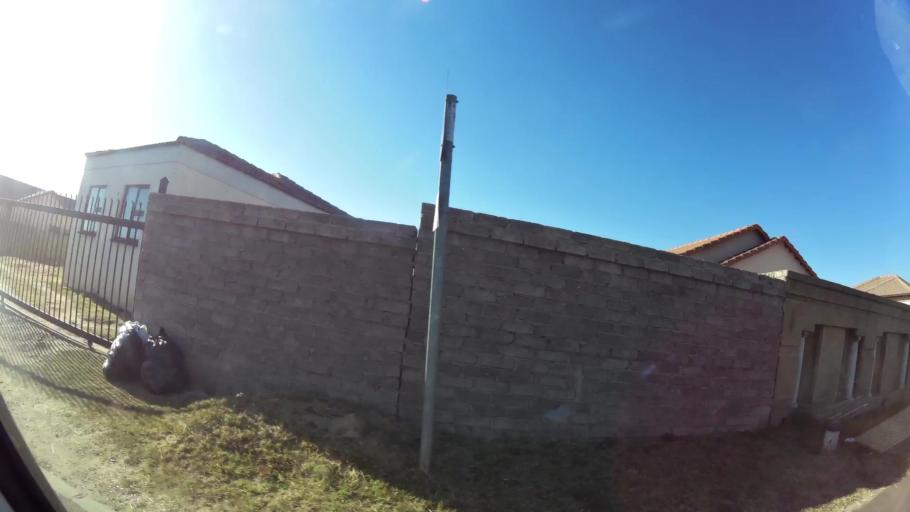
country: ZA
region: Gauteng
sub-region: City of Johannesburg Metropolitan Municipality
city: Diepsloot
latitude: -25.8957
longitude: 28.0948
